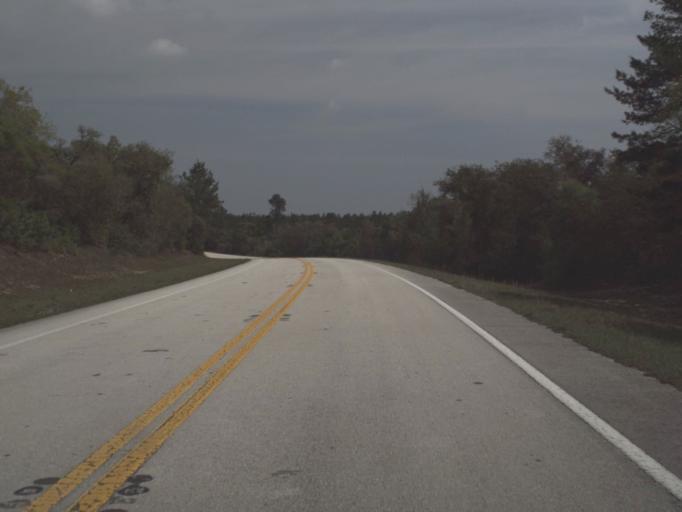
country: US
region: Florida
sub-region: Lake County
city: Astor
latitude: 29.2181
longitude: -81.6470
